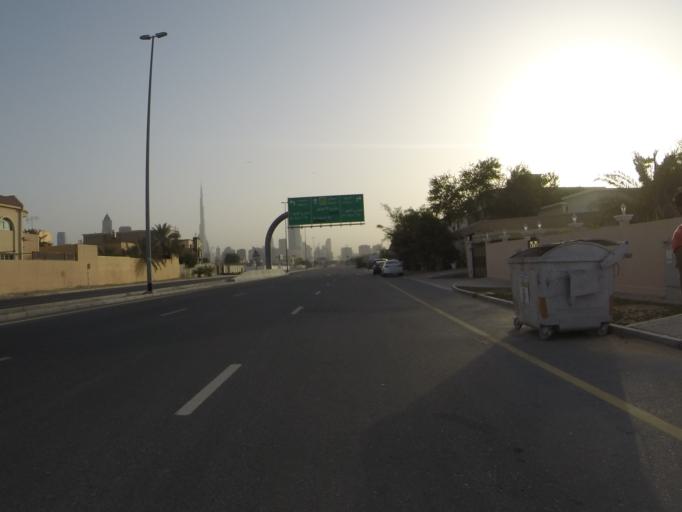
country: AE
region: Dubai
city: Dubai
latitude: 25.1641
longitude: 55.2586
